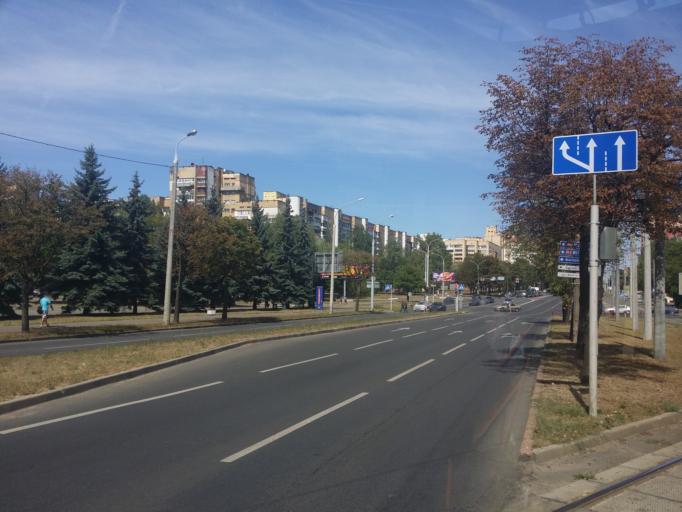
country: BY
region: Minsk
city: Minsk
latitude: 53.9379
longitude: 27.6049
